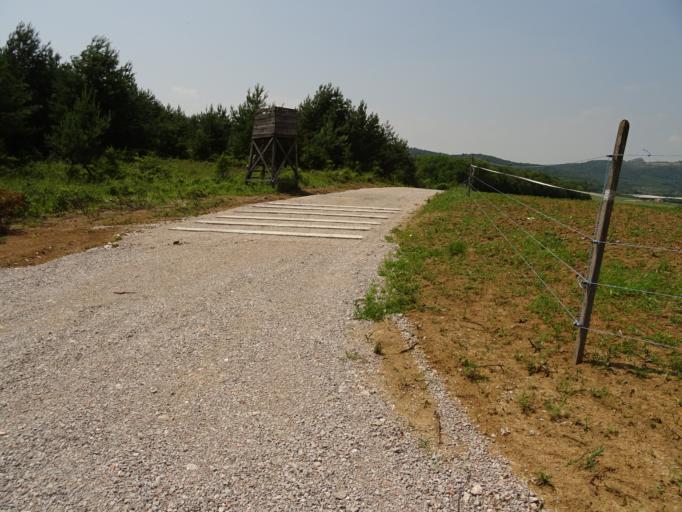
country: HU
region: Borsod-Abauj-Zemplen
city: Szendro
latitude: 48.5224
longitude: 20.7999
